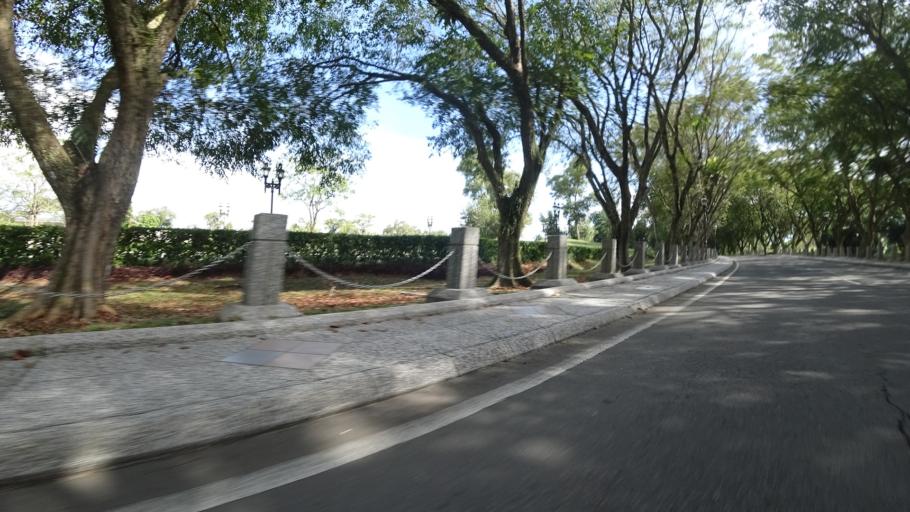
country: BN
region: Brunei and Muara
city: Bandar Seri Begawan
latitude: 4.9428
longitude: 114.8334
